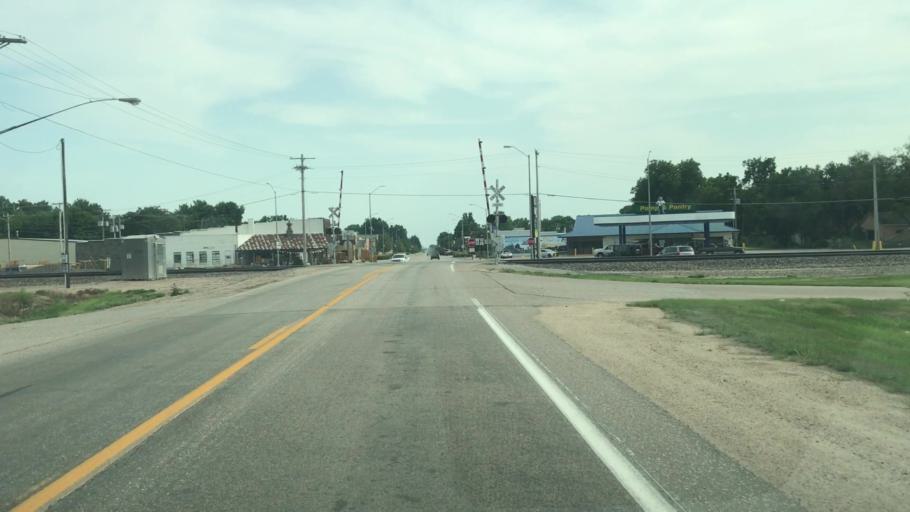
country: US
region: Nebraska
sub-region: Hall County
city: Wood River
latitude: 41.0029
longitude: -98.6074
